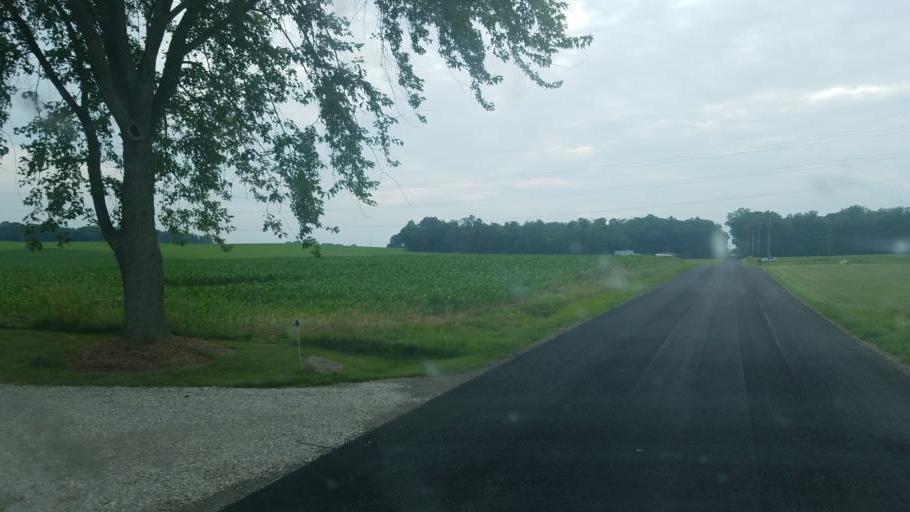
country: US
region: Ohio
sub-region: Wayne County
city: Apple Creek
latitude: 40.7773
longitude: -81.8868
